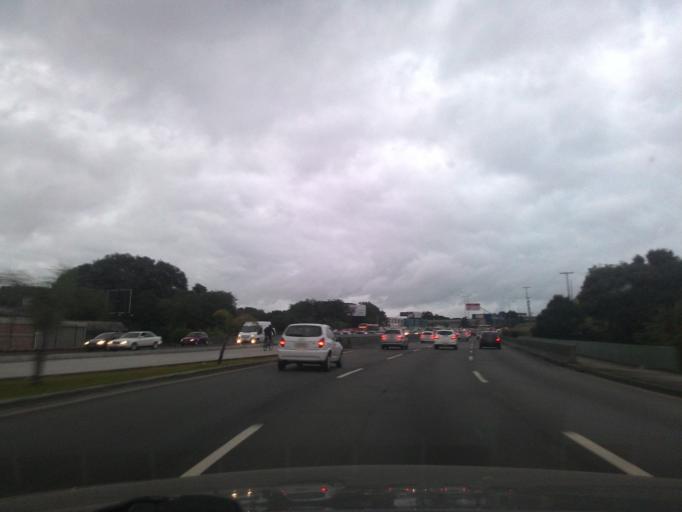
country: BR
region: Parana
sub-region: Curitiba
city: Curitiba
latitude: -25.4575
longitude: -49.2491
